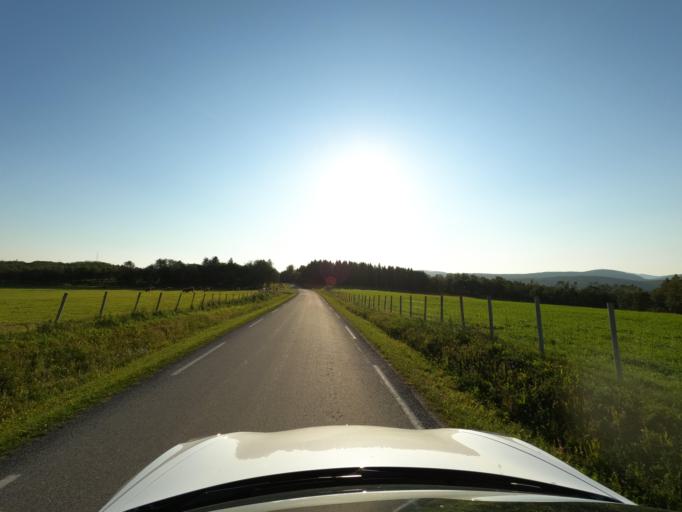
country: NO
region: Troms
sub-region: Skanland
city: Evenskjer
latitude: 68.4594
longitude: 16.6912
